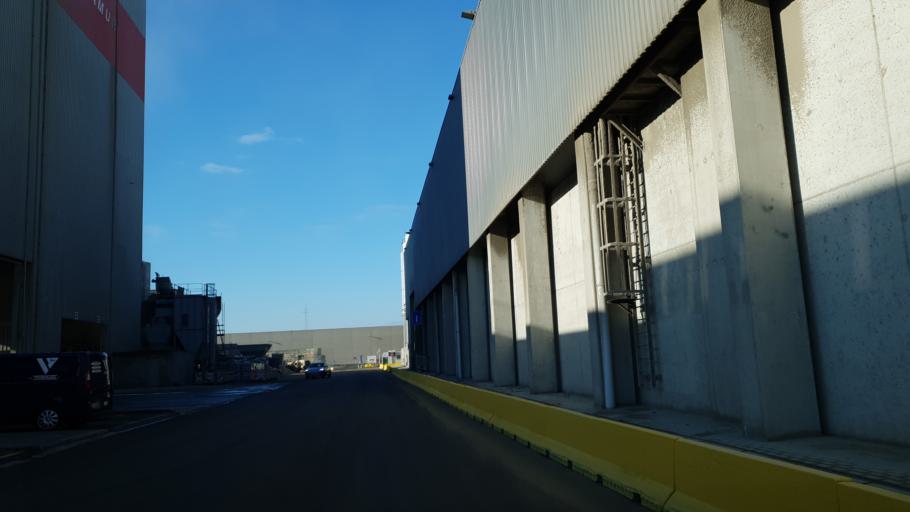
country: BE
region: Flanders
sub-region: Provincie Antwerpen
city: Zwijndrecht
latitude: 51.2451
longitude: 4.3608
